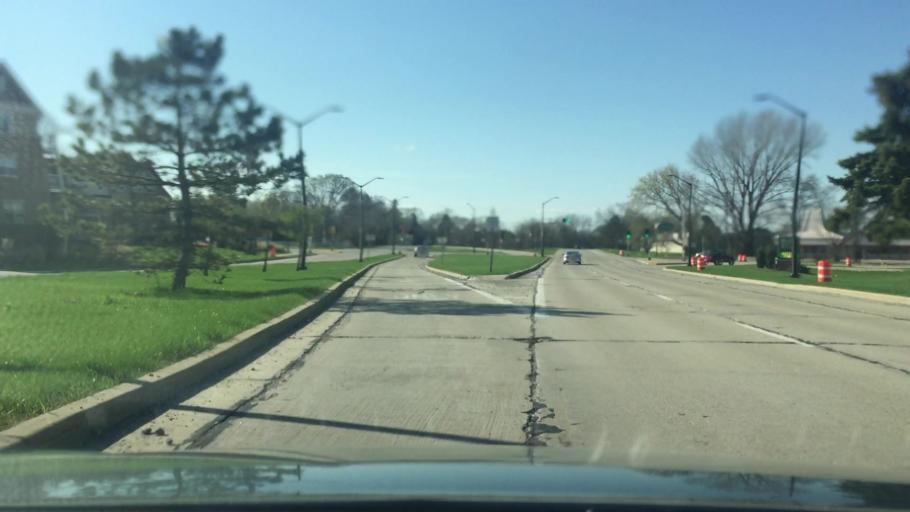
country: US
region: Wisconsin
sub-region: Milwaukee County
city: Brown Deer
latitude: 43.1621
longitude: -87.9622
